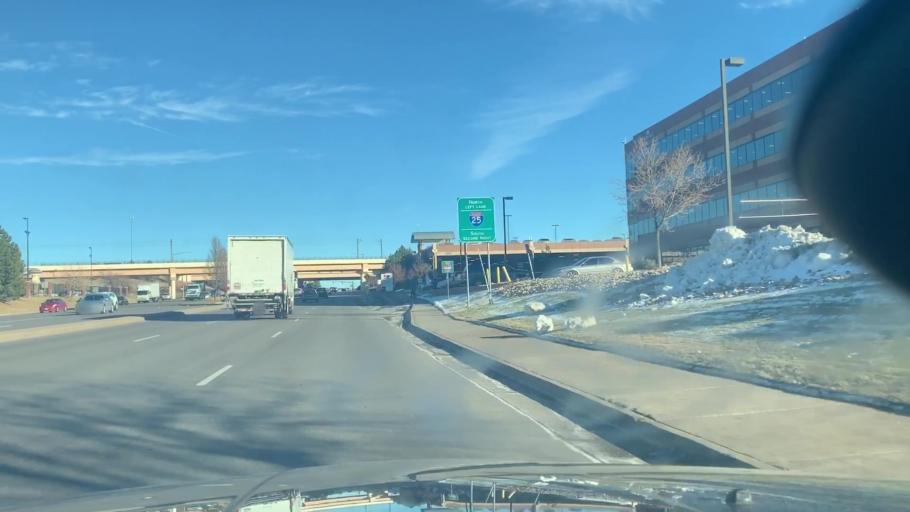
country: US
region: Colorado
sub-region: Arapahoe County
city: Centennial
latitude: 39.5804
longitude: -104.8804
